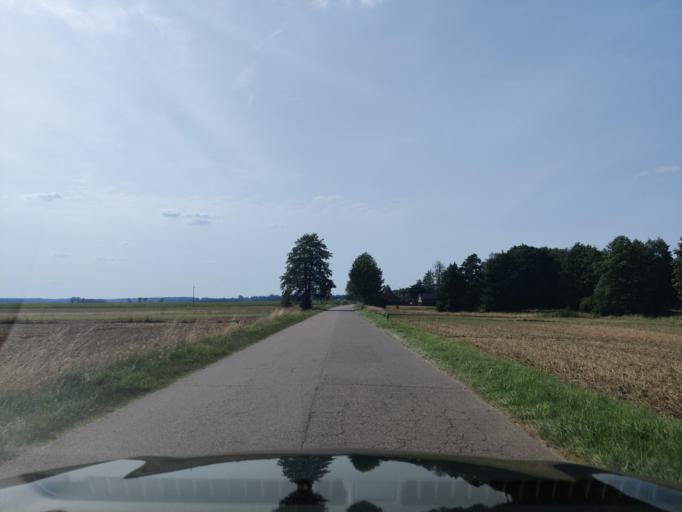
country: PL
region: Masovian Voivodeship
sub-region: Powiat pultuski
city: Obryte
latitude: 52.7684
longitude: 21.2775
